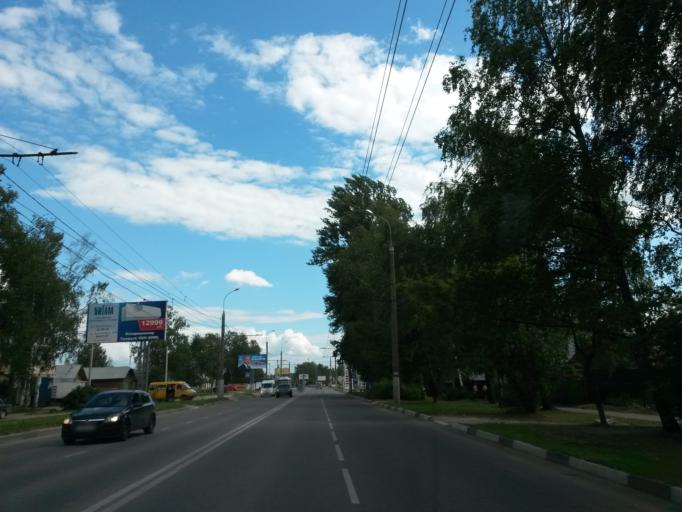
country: RU
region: Ivanovo
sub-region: Gorod Ivanovo
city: Ivanovo
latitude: 56.9804
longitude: 40.9998
